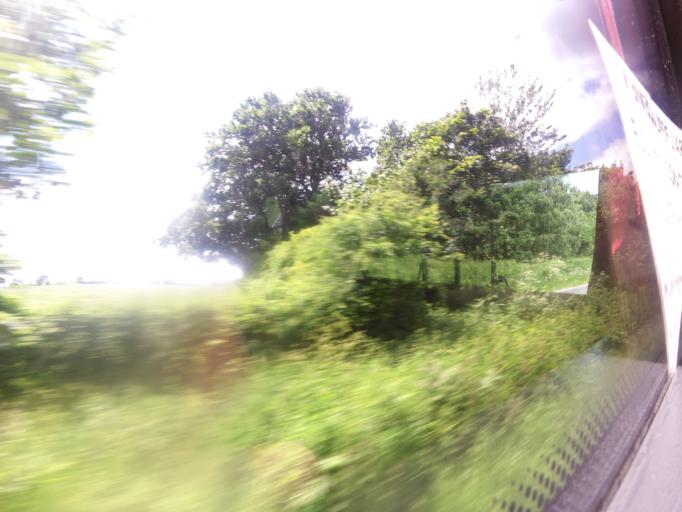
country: GB
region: England
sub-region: Norfolk
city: Sheringham
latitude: 52.9227
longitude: 1.2149
